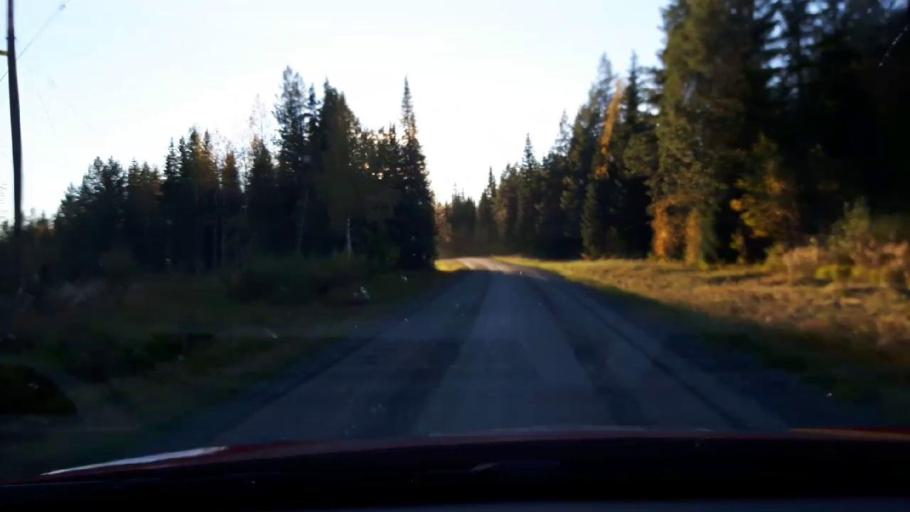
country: SE
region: Jaemtland
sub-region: OEstersunds Kommun
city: Lit
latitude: 63.4138
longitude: 14.6782
